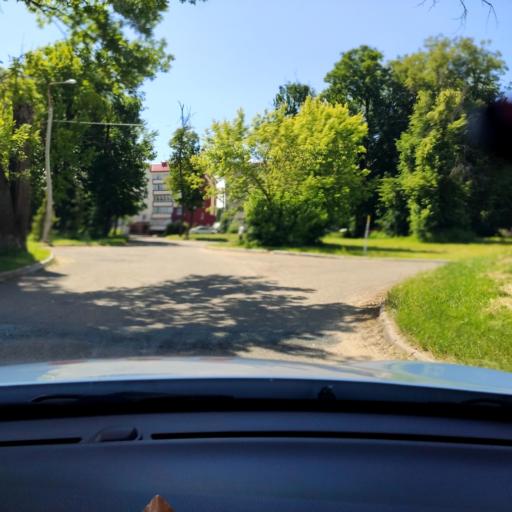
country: RU
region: Tatarstan
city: Sviyazhsk
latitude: 55.7785
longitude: 48.7903
